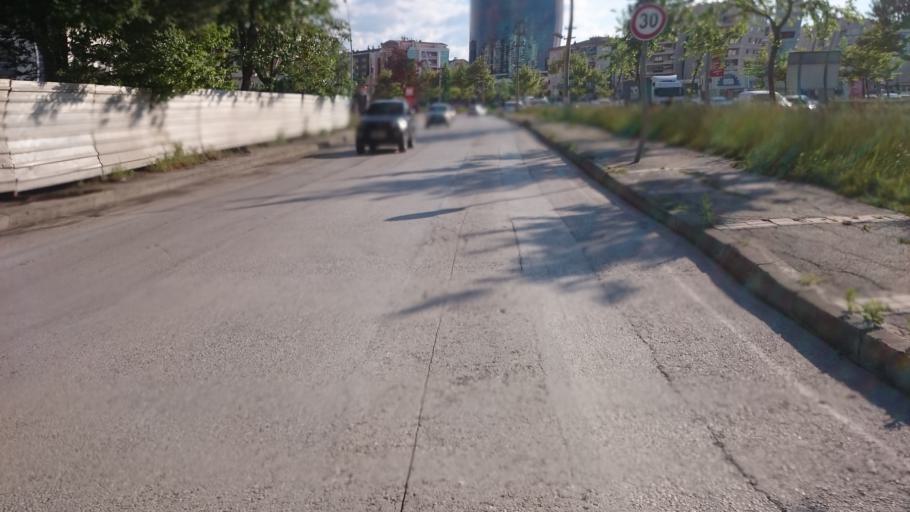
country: TR
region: Bursa
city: Cali
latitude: 40.2210
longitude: 28.9541
